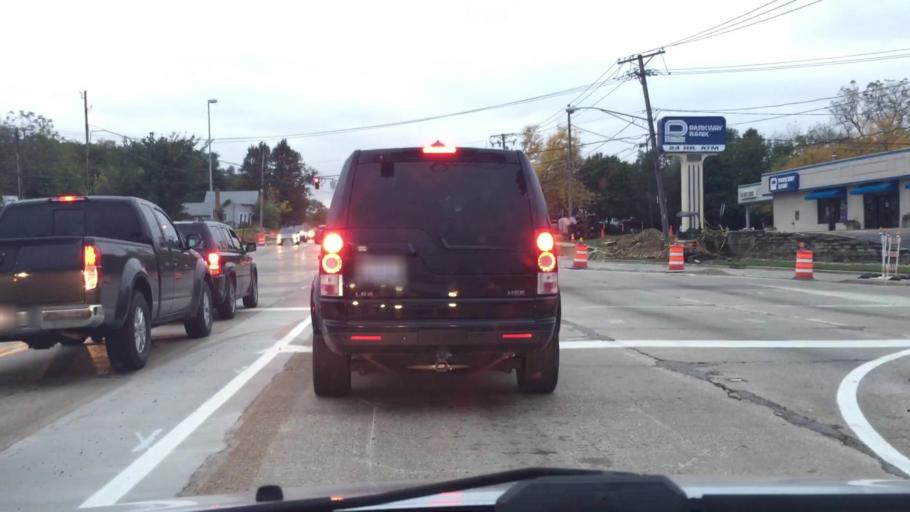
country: US
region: Illinois
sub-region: Kane County
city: West Dundee
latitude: 42.1076
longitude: -88.2934
